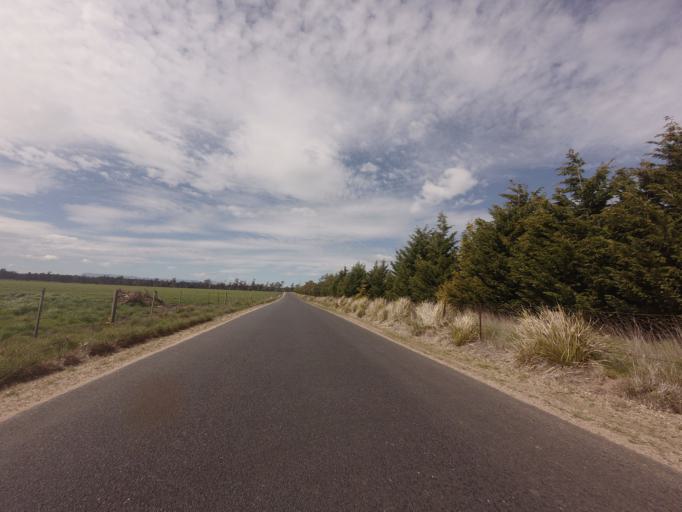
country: AU
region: Tasmania
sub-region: Northern Midlands
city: Longford
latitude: -41.6628
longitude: 147.1861
